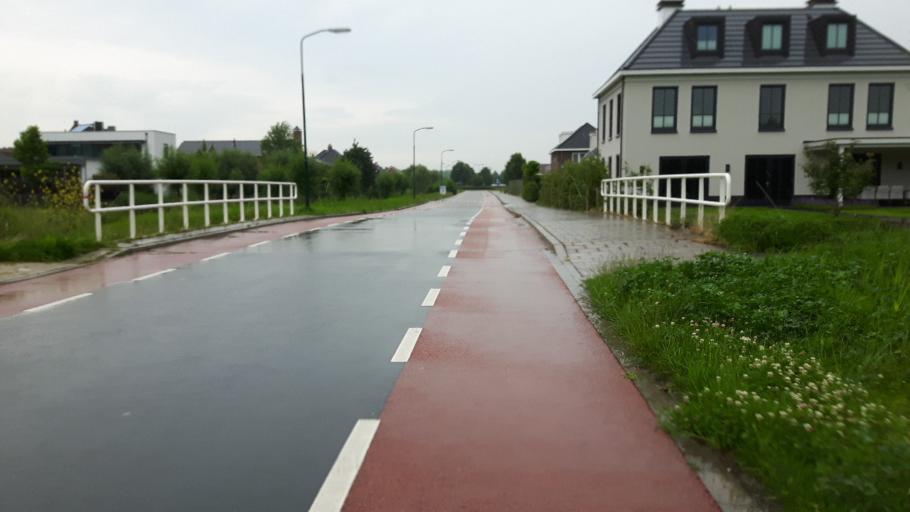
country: NL
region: Utrecht
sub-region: Gemeente Montfoort
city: Montfoort
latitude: 52.0371
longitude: 4.9588
